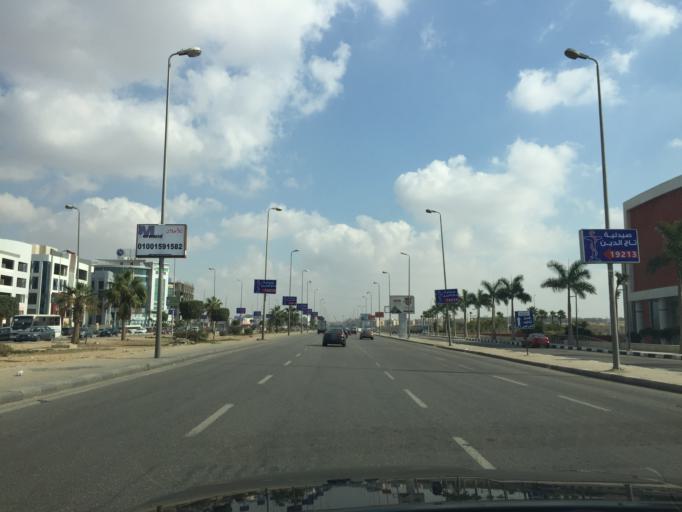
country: EG
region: Muhafazat al Qalyubiyah
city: Al Khankah
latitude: 30.0254
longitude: 31.4645
